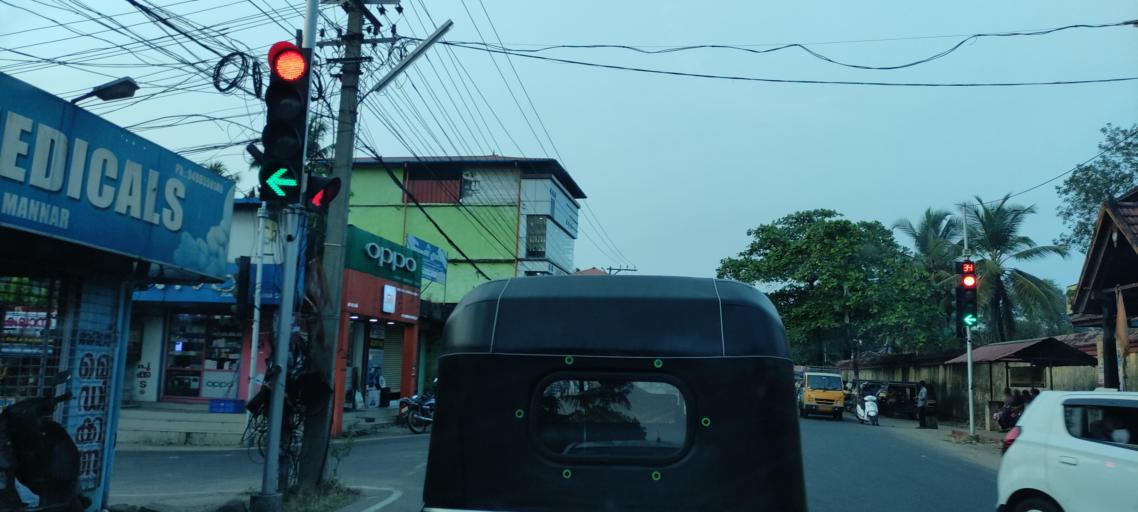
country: IN
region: Kerala
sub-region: Alappuzha
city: Mavelikara
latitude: 9.3195
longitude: 76.5335
